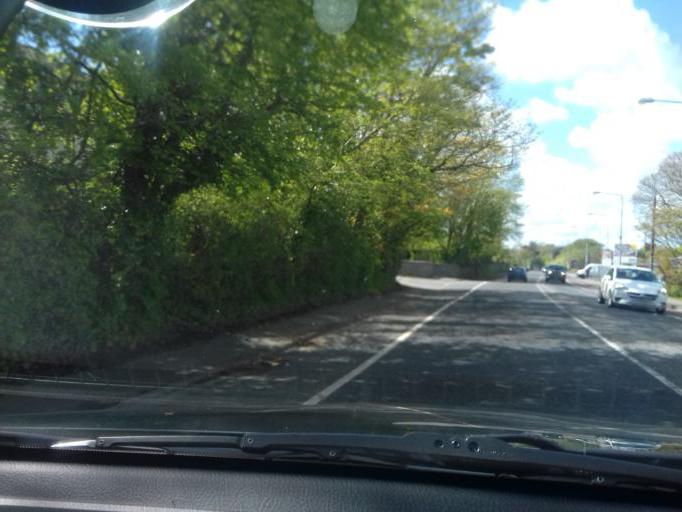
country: IE
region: Munster
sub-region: Waterford
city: Waterford
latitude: 52.2378
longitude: -7.0627
